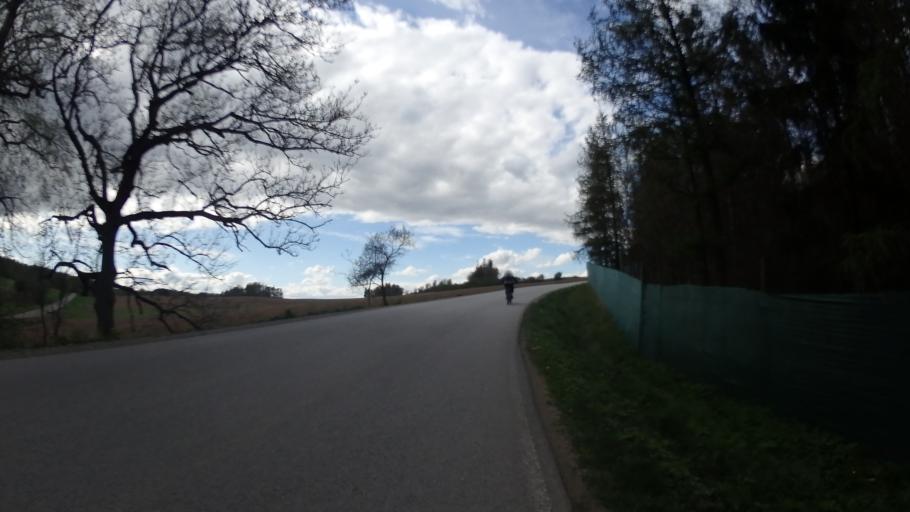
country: CZ
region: Vysocina
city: Merin
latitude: 49.3647
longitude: 15.9013
